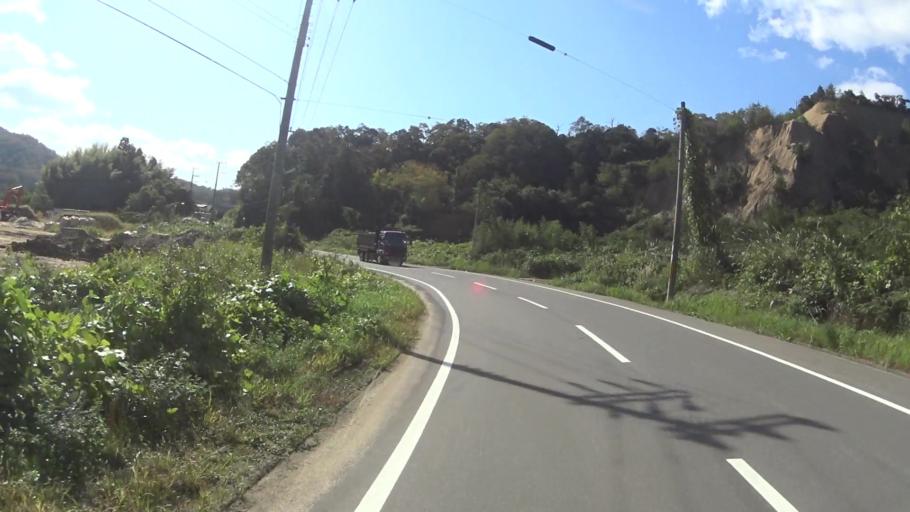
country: JP
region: Kyoto
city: Miyazu
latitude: 35.6991
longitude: 135.1012
